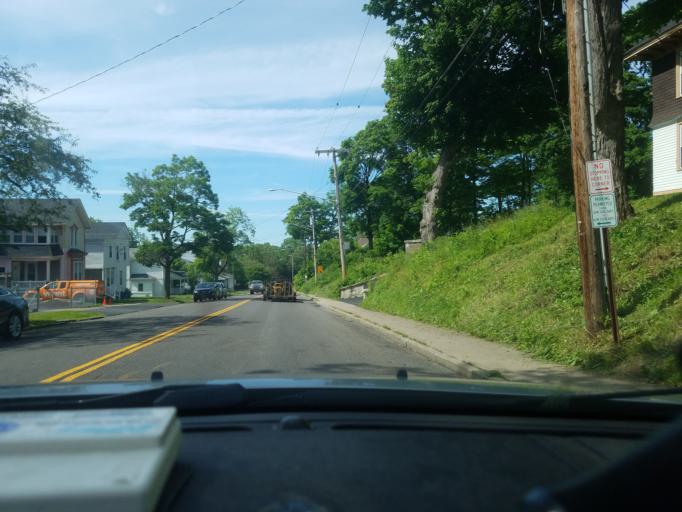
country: US
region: New York
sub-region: Onondaga County
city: Syracuse
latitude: 43.0457
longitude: -76.1197
